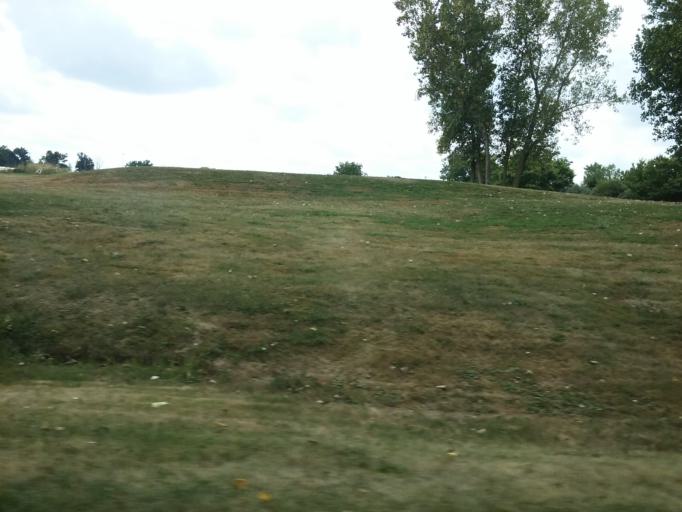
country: US
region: Ohio
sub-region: Hancock County
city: Findlay
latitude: 41.0510
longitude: -83.6708
